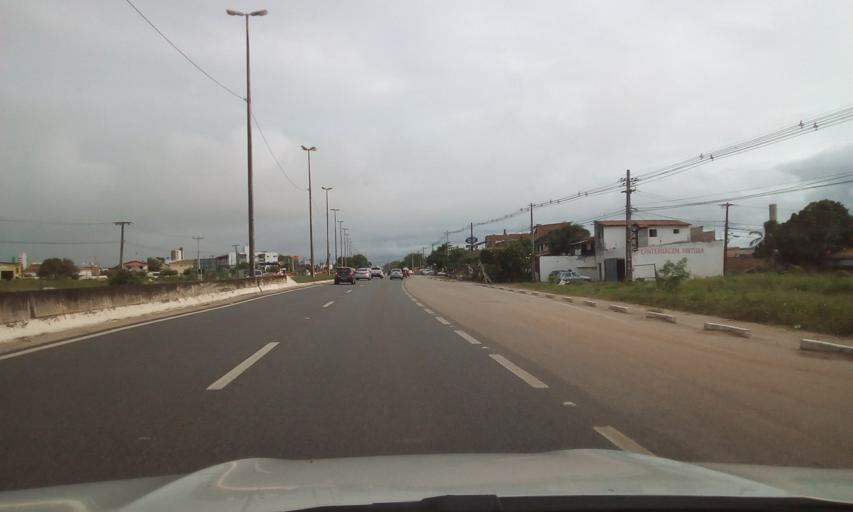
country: BR
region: Paraiba
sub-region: Cabedelo
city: Cabedelo
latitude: -7.0184
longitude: -34.8351
